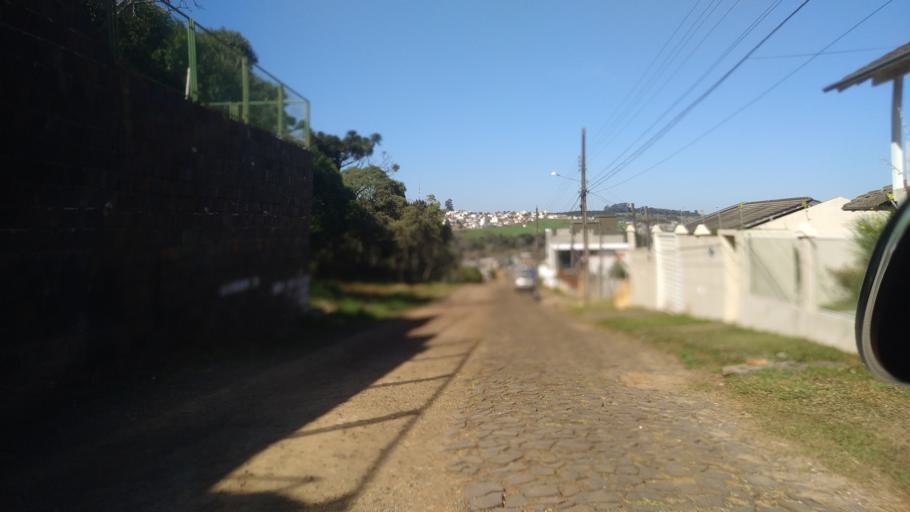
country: BR
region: Santa Catarina
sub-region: Chapeco
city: Chapeco
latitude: -27.0910
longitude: -52.5891
